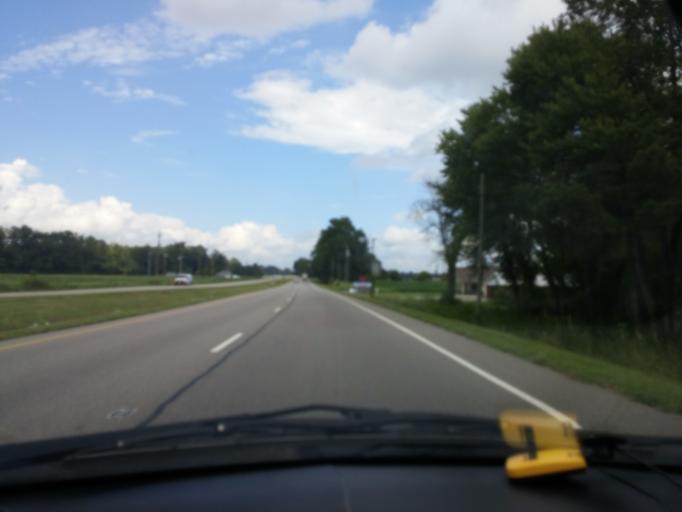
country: US
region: North Carolina
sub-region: Pitt County
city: Grifton
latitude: 35.3507
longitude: -77.4675
